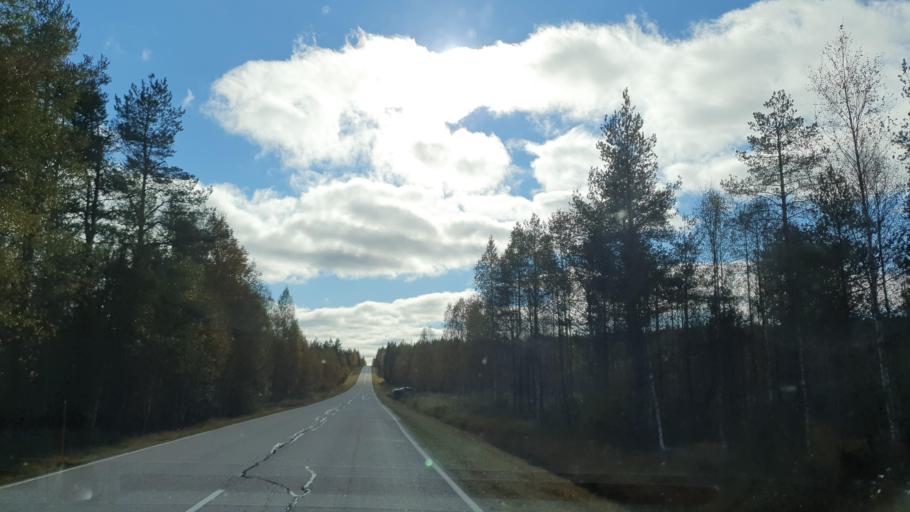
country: FI
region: Kainuu
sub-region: Kehys-Kainuu
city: Puolanka
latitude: 65.1149
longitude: 27.7076
